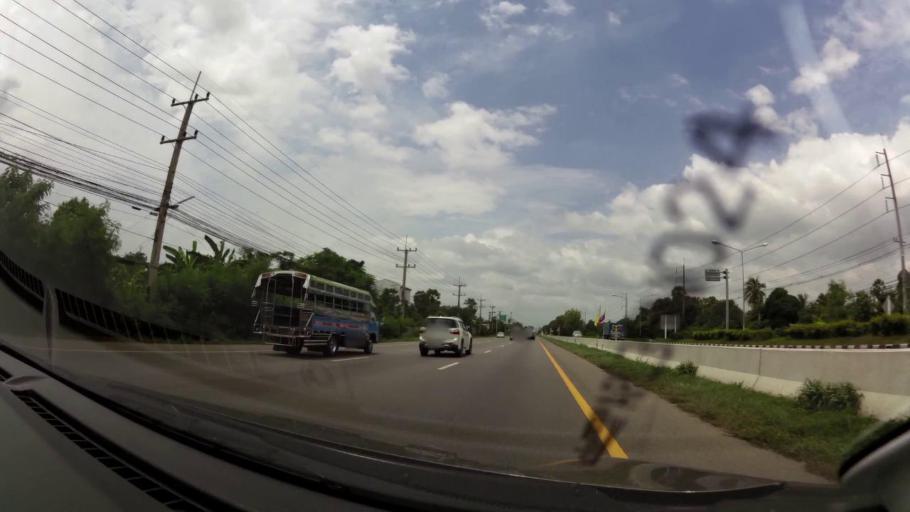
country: TH
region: Phetchaburi
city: Khao Yoi
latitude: 13.1589
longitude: 99.8465
